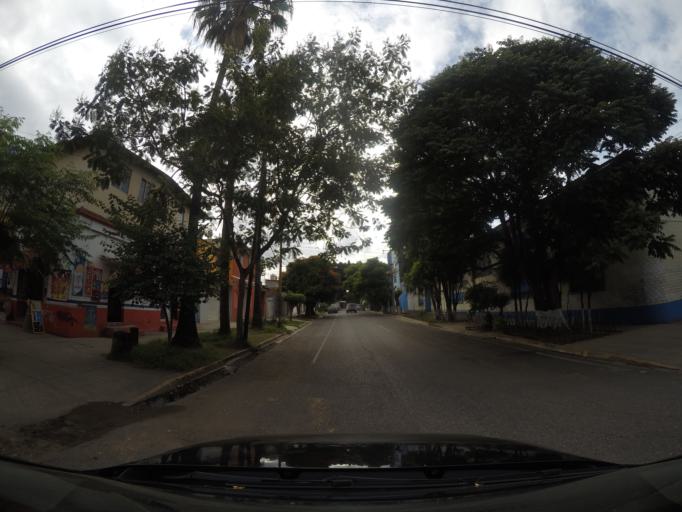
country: MX
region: Oaxaca
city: Oaxaca de Juarez
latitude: 17.0766
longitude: -96.7171
